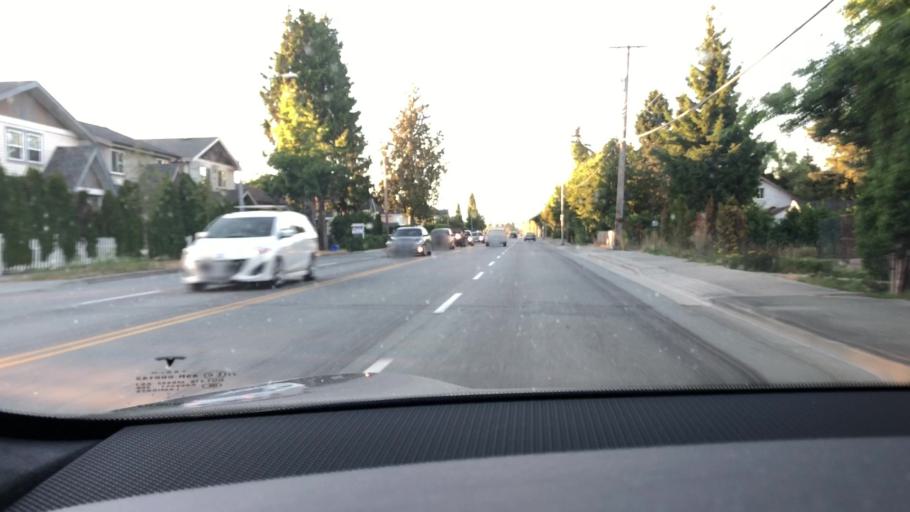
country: CA
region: British Columbia
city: Richmond
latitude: 49.1670
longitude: -123.1140
